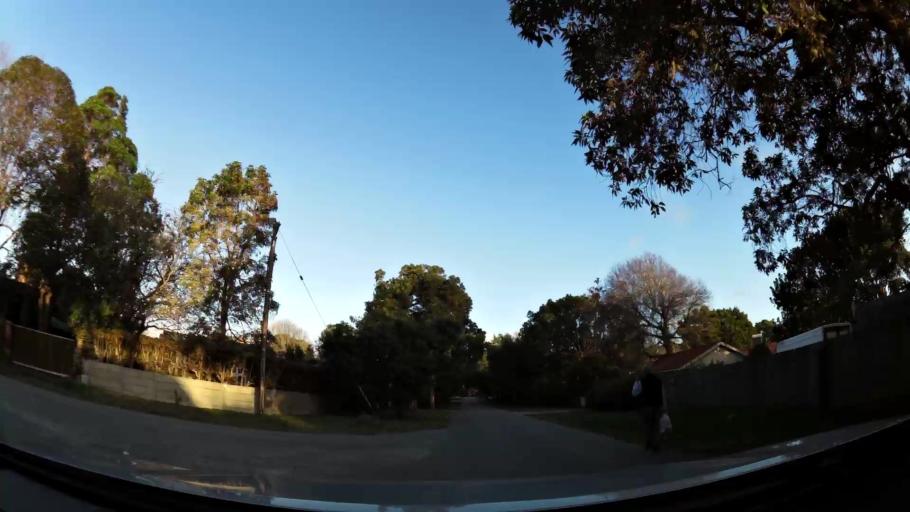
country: ZA
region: Western Cape
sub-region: Eden District Municipality
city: Knysna
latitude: -34.0181
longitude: 22.8039
